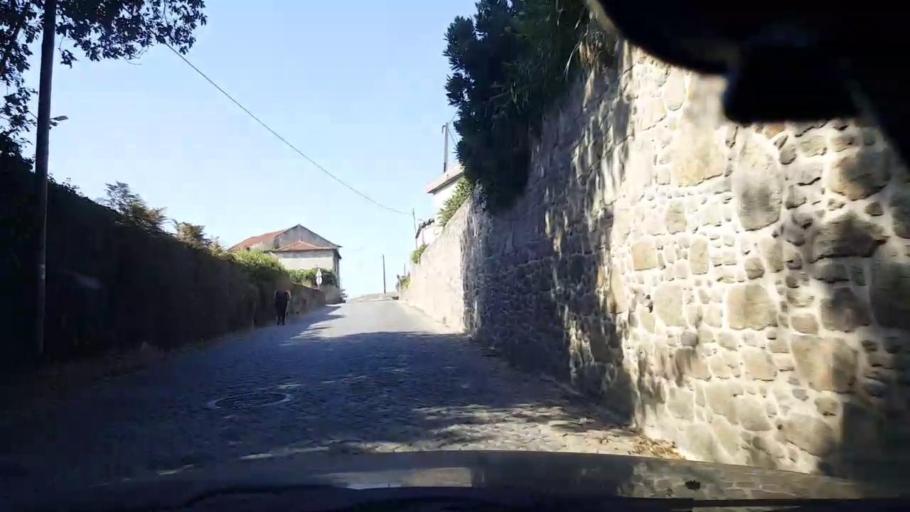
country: PT
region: Porto
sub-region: Vila do Conde
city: Arvore
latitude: 41.3899
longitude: -8.6888
